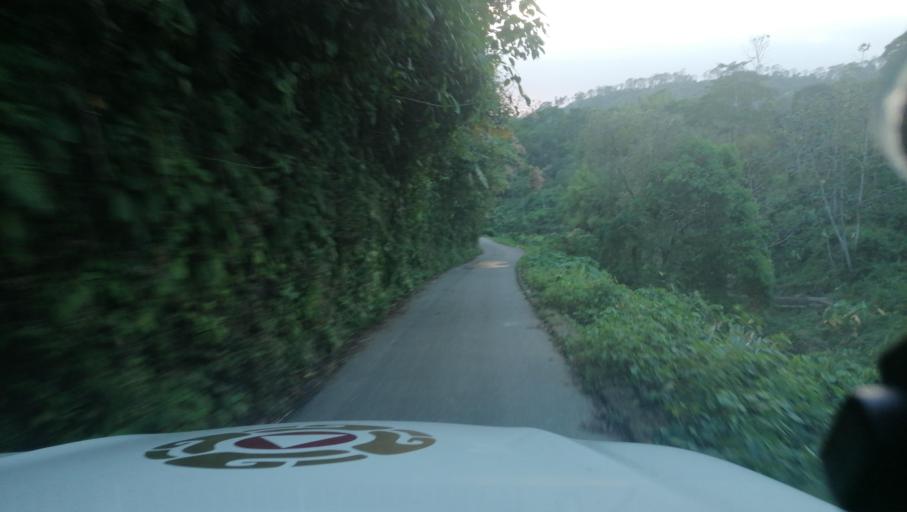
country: MX
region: Chiapas
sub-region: Cacahoatan
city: Benito Juarez
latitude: 15.0688
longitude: -92.2327
